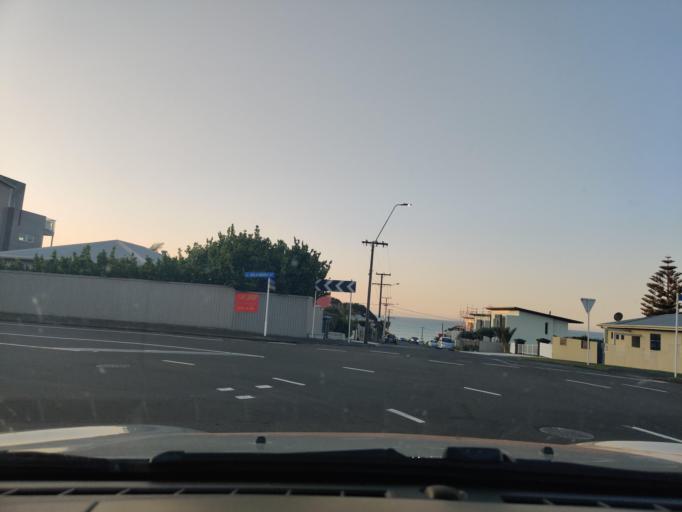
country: NZ
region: Taranaki
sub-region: New Plymouth District
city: New Plymouth
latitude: -39.0525
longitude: 174.0856
